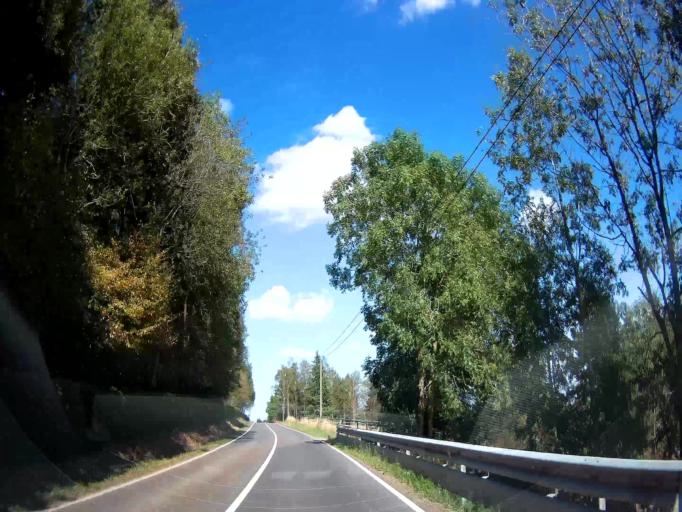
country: BE
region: Wallonia
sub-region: Province de Namur
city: Houyet
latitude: 50.1834
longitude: 4.9310
